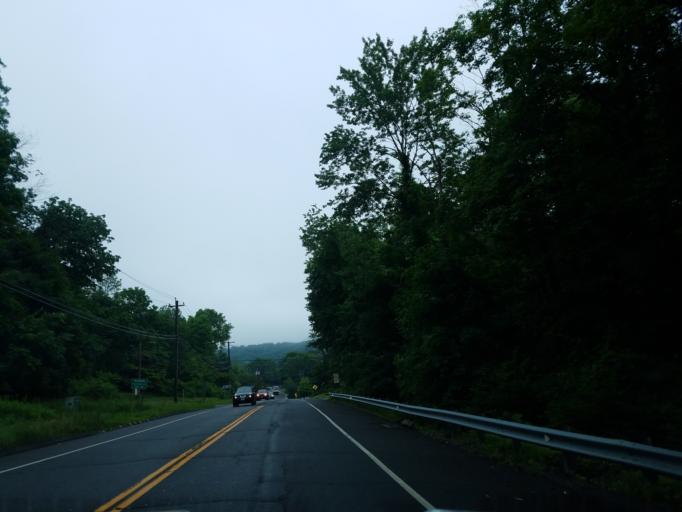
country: US
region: Connecticut
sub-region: Fairfield County
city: Georgetown
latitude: 41.2551
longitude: -73.4266
